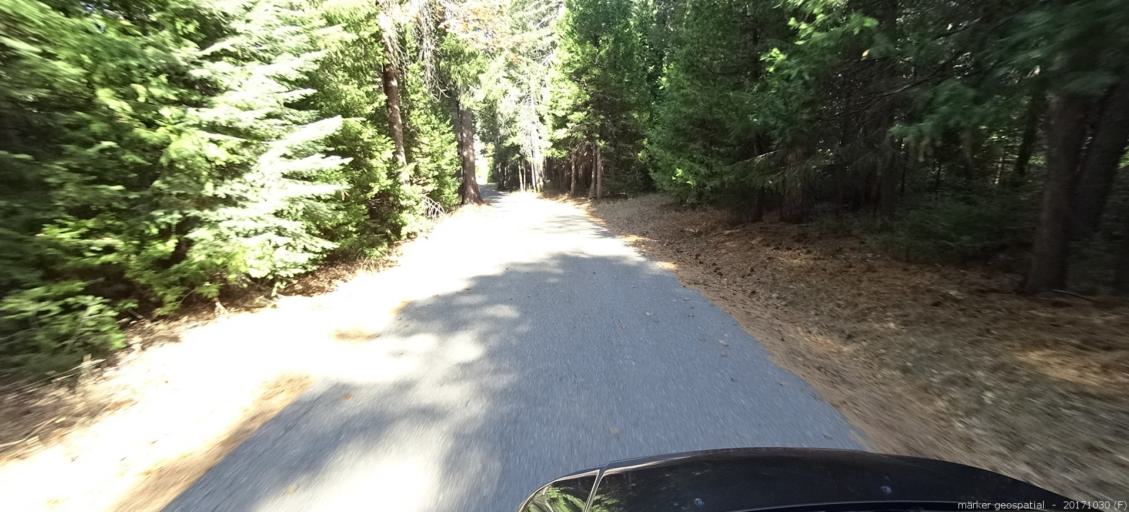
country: US
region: California
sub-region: Shasta County
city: Shingletown
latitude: 40.5189
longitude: -121.6888
